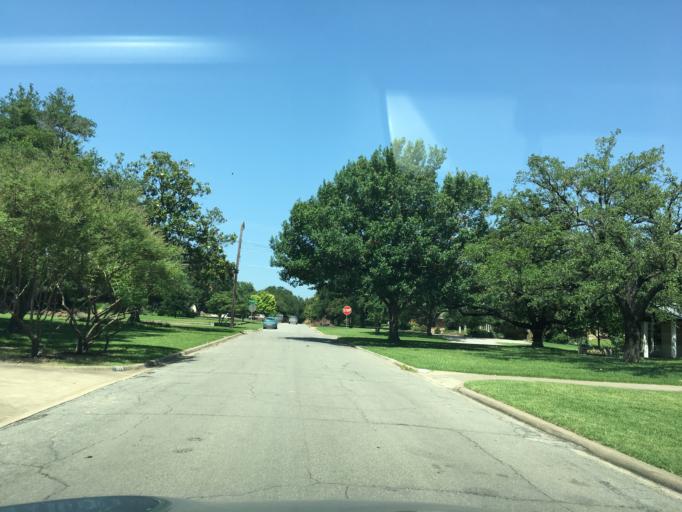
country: US
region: Texas
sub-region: Dallas County
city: University Park
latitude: 32.8989
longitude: -96.7831
